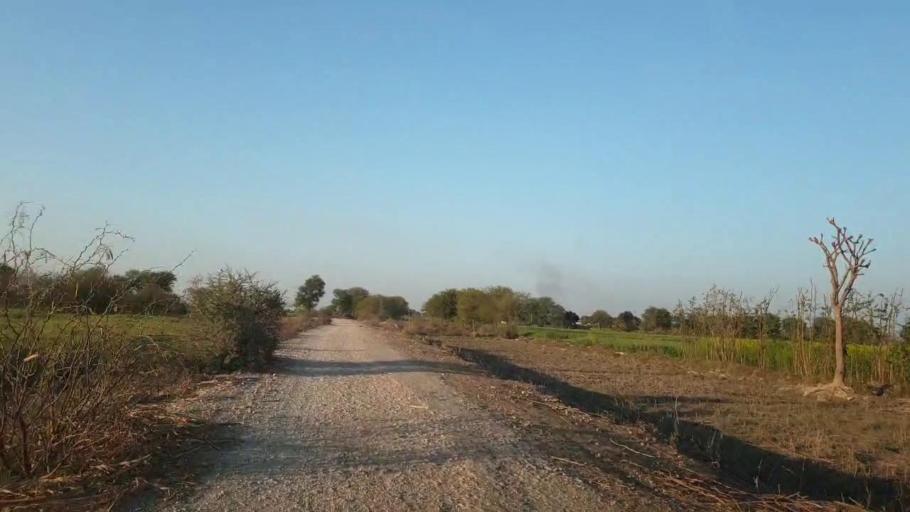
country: PK
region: Sindh
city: Mirpur Khas
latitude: 25.6930
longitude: 69.0508
